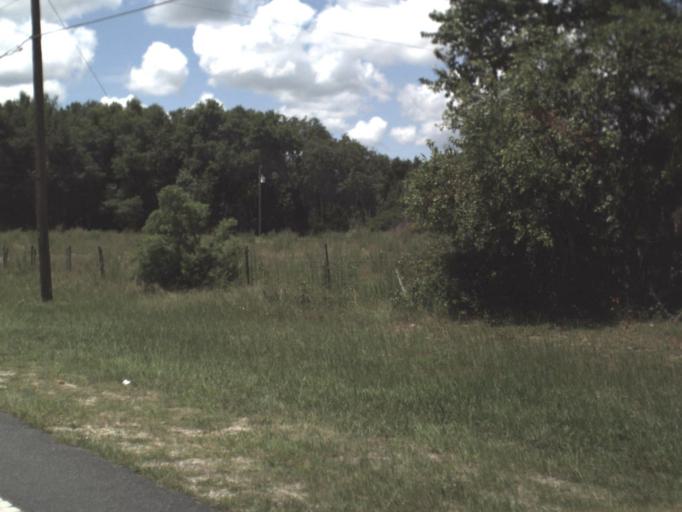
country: US
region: Florida
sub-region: Alachua County
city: Hawthorne
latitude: 29.6604
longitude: -82.0329
